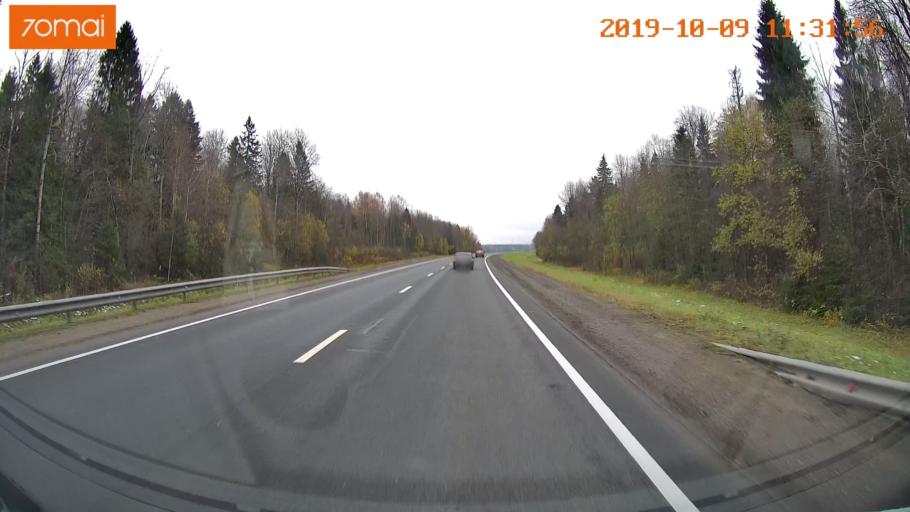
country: RU
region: Vologda
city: Gryazovets
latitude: 59.0409
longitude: 40.1039
